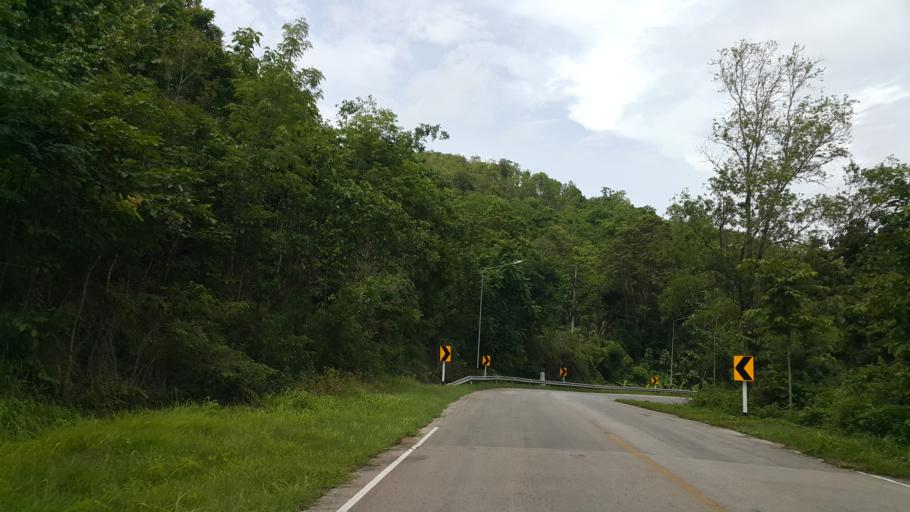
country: TH
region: Lampang
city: Mueang Pan
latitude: 18.7788
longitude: 99.5367
